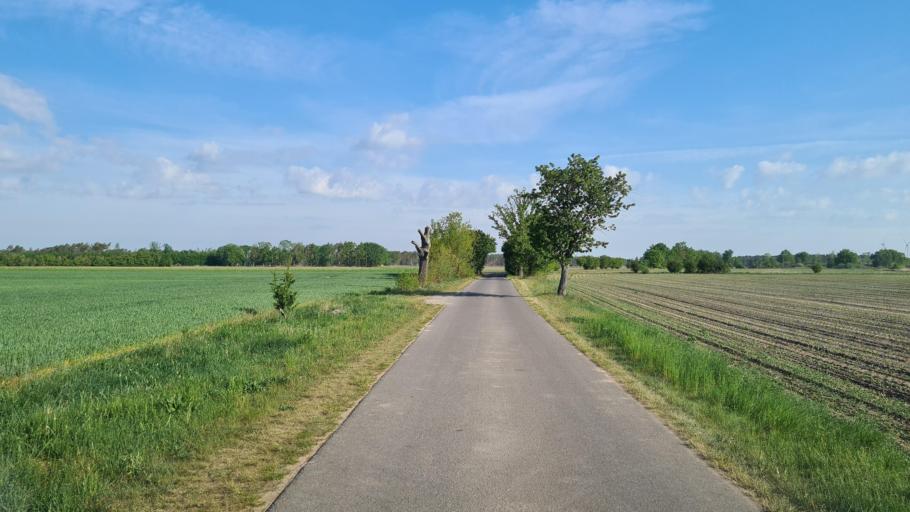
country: DE
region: Brandenburg
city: Falkenberg
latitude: 51.5889
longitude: 13.2055
